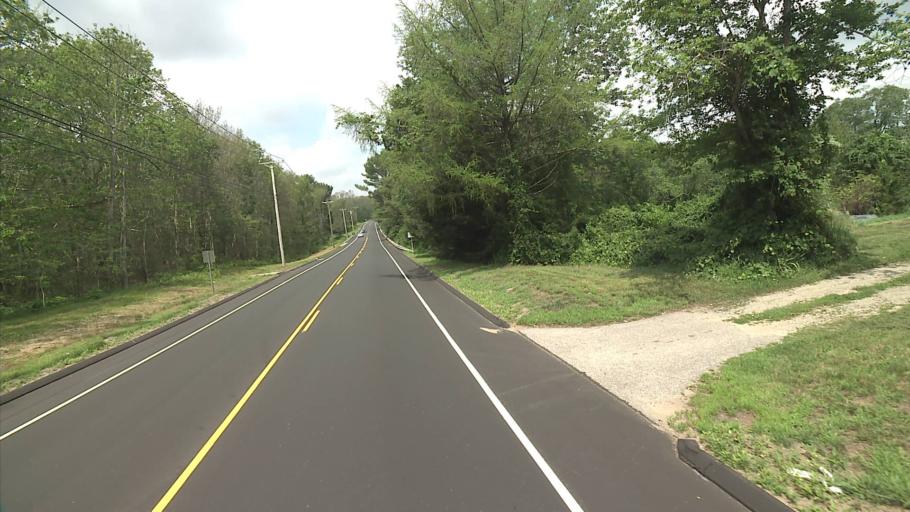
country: US
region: Connecticut
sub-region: New London County
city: Preston City
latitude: 41.5752
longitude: -71.8830
